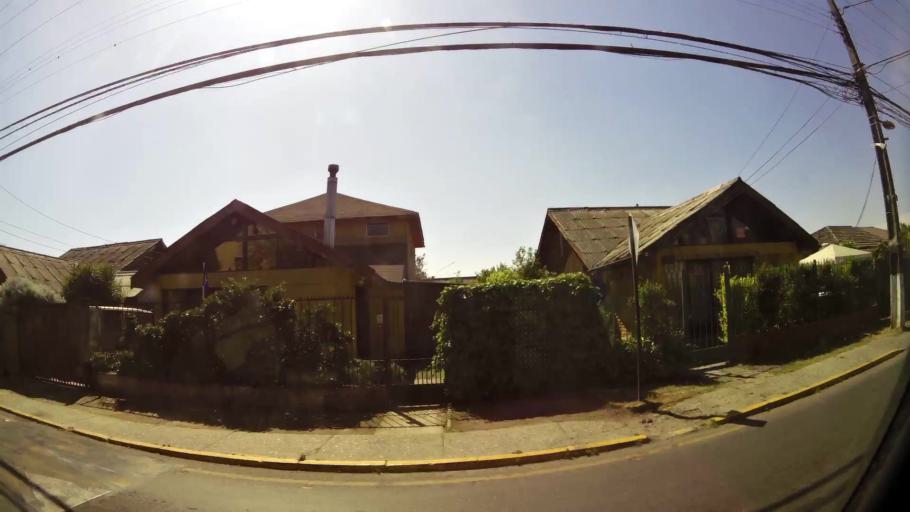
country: CL
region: Santiago Metropolitan
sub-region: Provincia de Santiago
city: Lo Prado
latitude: -33.5161
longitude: -70.7497
